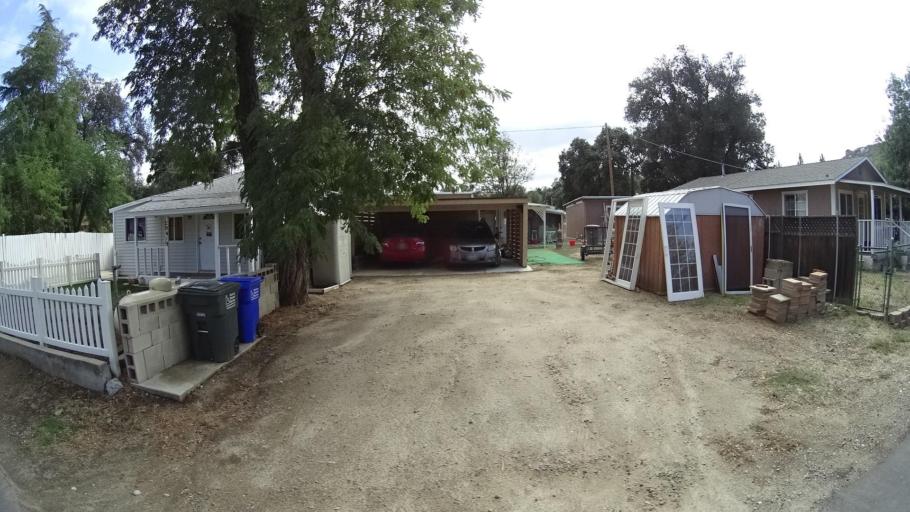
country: US
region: California
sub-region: San Diego County
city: Campo
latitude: 32.6792
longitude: -116.5126
